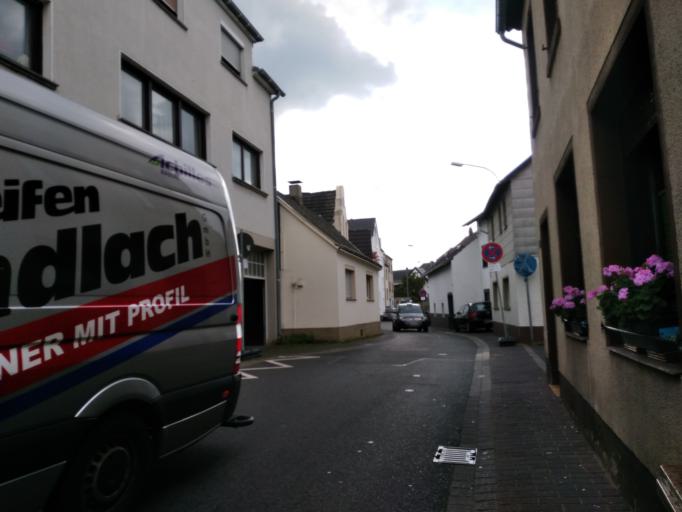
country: DE
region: North Rhine-Westphalia
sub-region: Regierungsbezirk Koln
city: Bad Honnef
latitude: 50.6402
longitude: 7.2353
